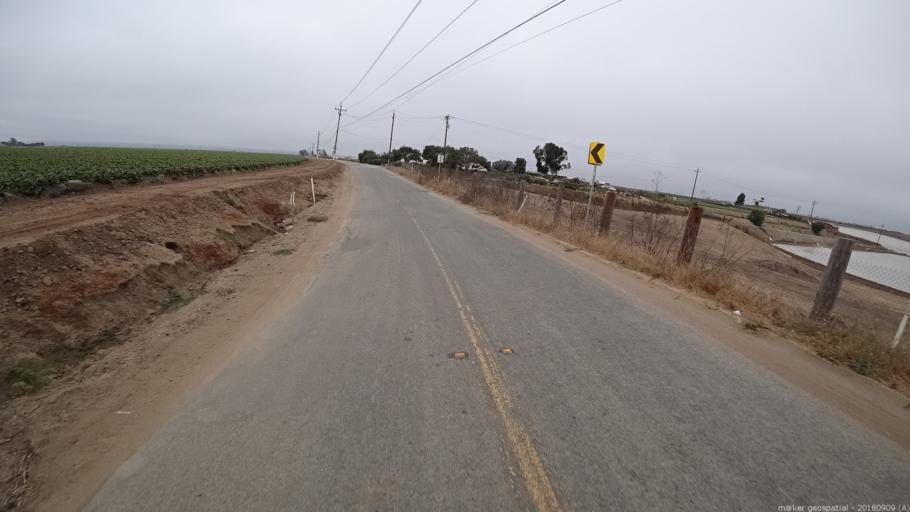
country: US
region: California
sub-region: Monterey County
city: Boronda
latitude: 36.7264
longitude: -121.6723
